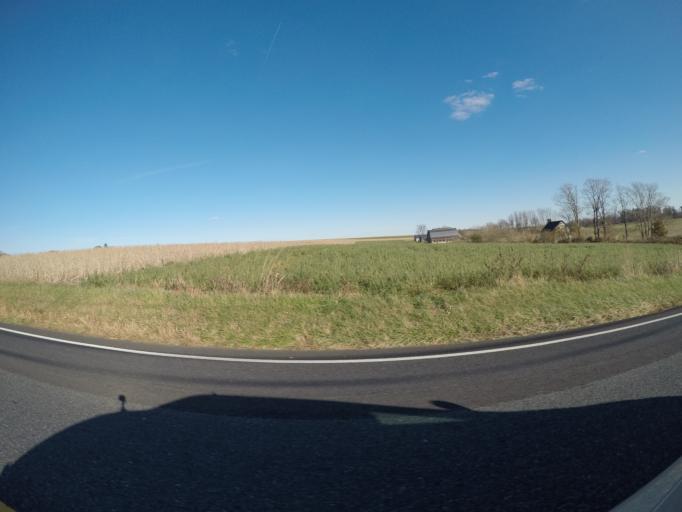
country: US
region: Maryland
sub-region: Harford County
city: South Bel Air
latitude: 39.6127
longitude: -76.2609
